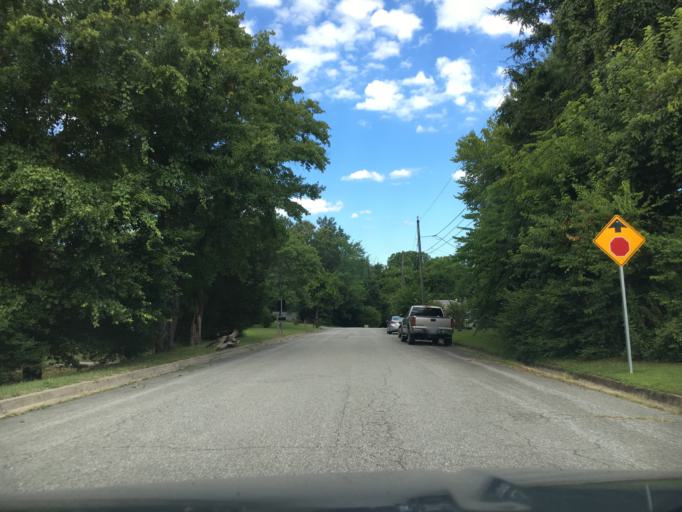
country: US
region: Virginia
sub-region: Halifax County
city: South Boston
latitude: 36.7143
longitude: -78.8970
